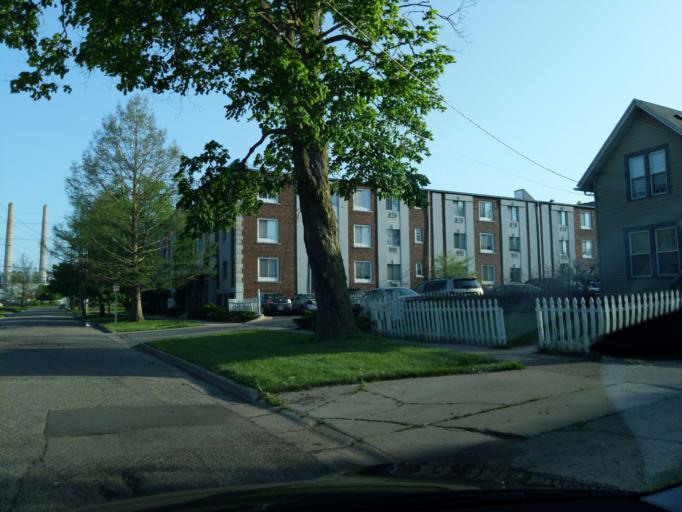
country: US
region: Michigan
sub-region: Ingham County
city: Lansing
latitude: 42.7284
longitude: -84.5586
